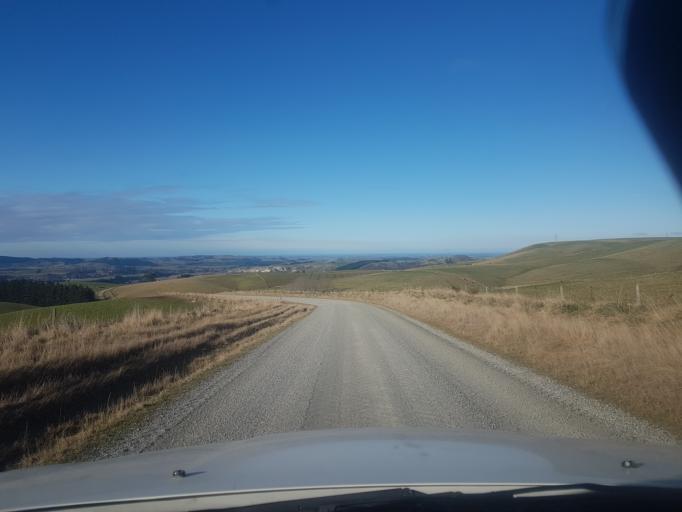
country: NZ
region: Canterbury
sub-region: Timaru District
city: Pleasant Point
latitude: -44.1674
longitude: 170.9053
